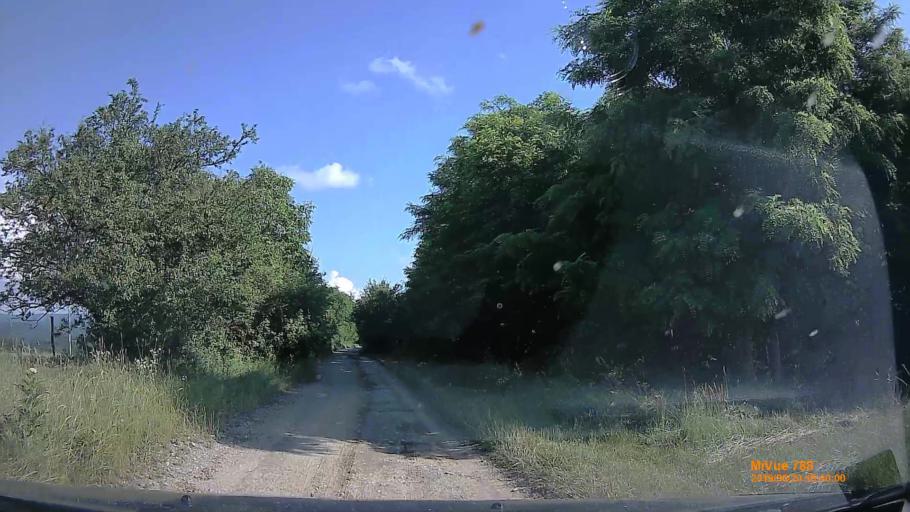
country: HU
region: Baranya
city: Buekkoesd
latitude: 46.1685
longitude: 18.0335
